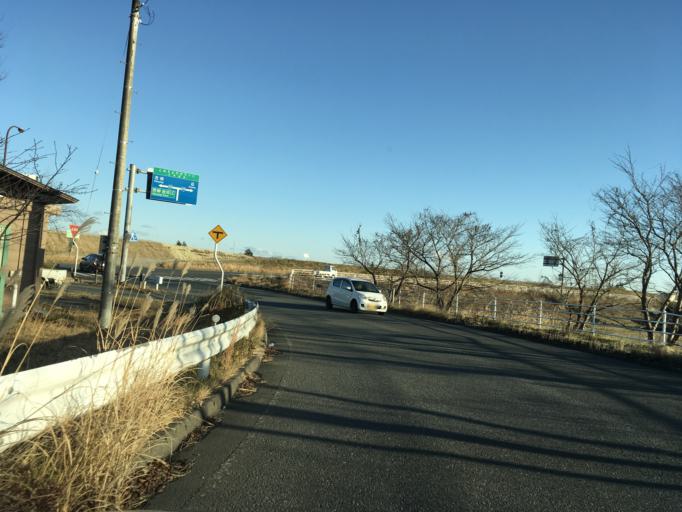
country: JP
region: Iwate
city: Ichinoseki
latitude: 38.7431
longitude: 141.1500
